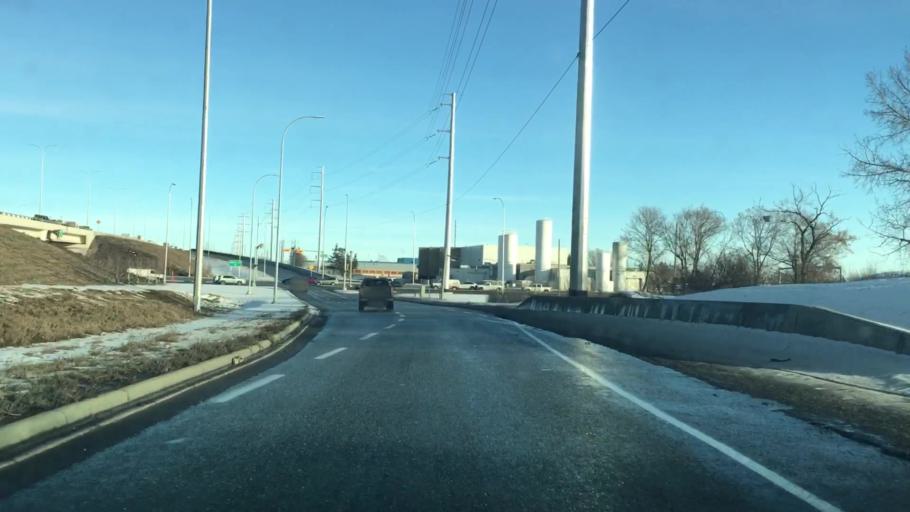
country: CA
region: Alberta
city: Calgary
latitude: 50.9787
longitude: -114.0011
